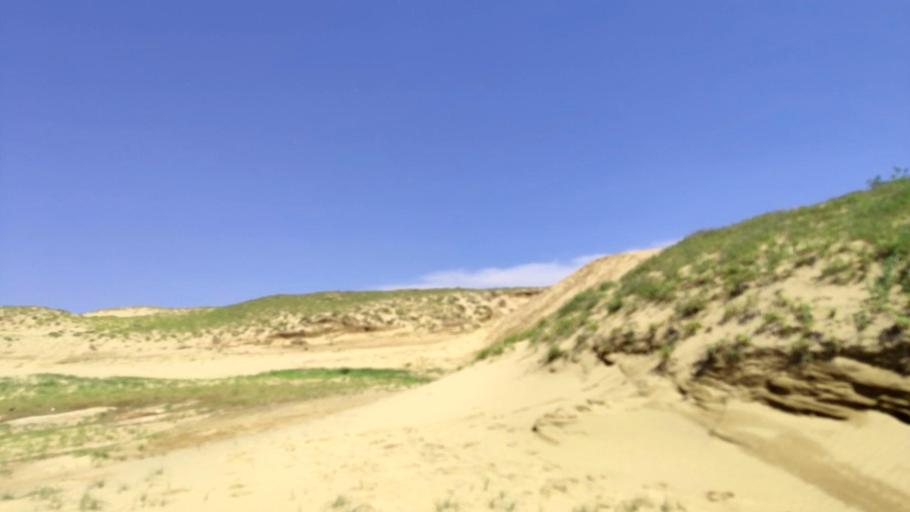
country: JP
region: Tottori
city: Tottori
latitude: 35.5425
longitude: 134.2324
